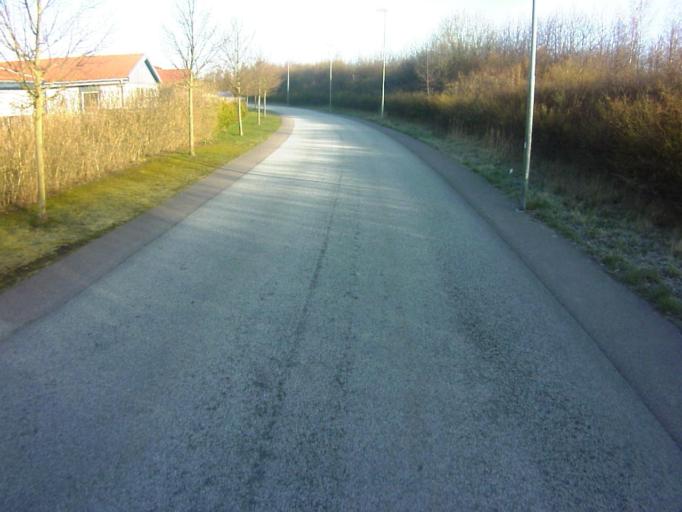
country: SE
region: Skane
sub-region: Kavlinge Kommun
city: Kaevlinge
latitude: 55.7968
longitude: 13.0972
